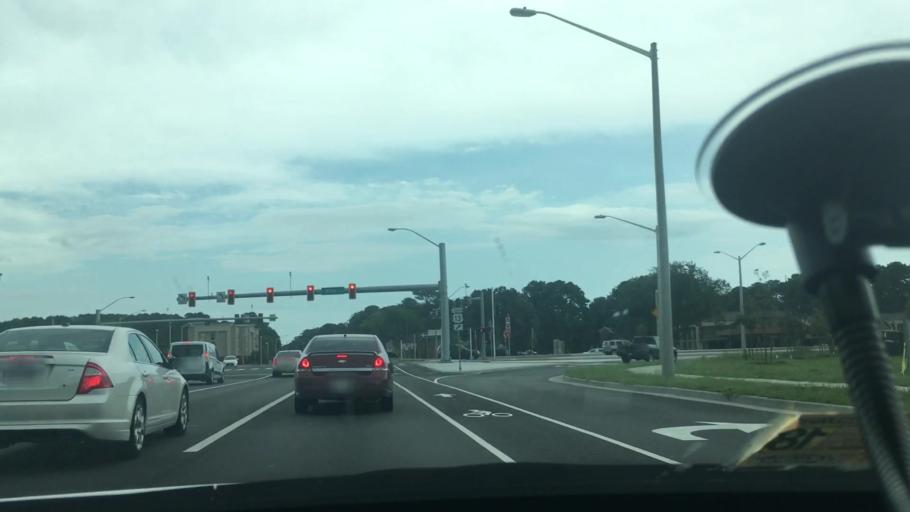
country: US
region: Virginia
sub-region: City of Norfolk
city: Norfolk
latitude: 36.8748
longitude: -76.2117
